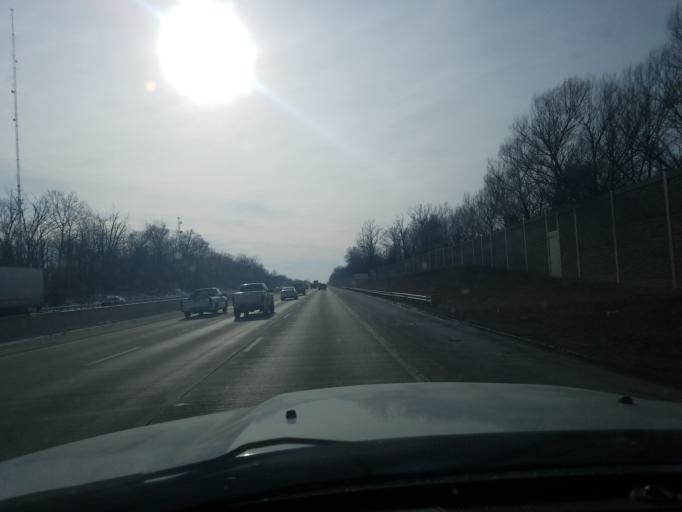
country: US
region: Indiana
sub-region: Allen County
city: Fort Wayne
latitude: 41.1147
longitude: -85.1947
